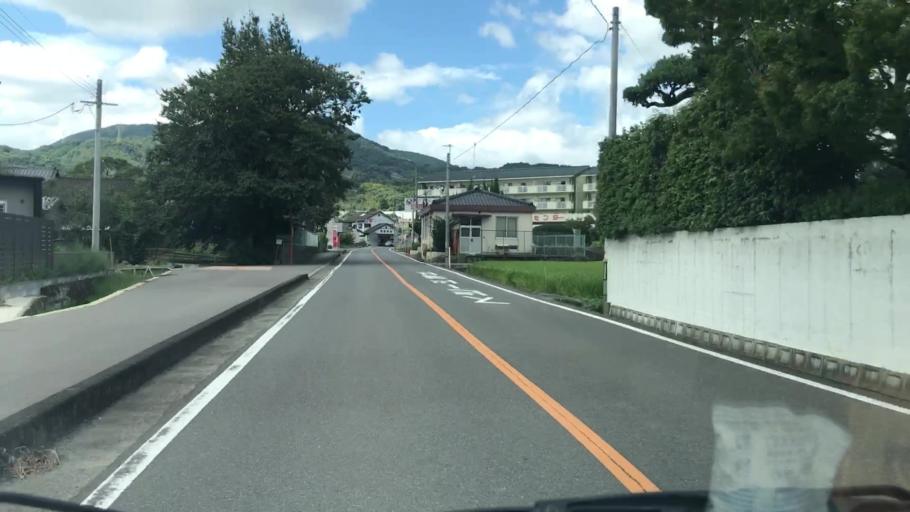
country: JP
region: Saga Prefecture
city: Takeocho-takeo
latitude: 33.2258
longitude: 130.1446
